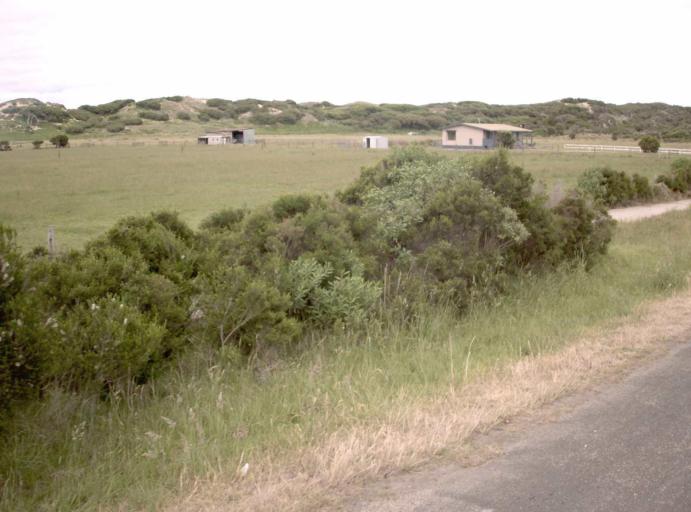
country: AU
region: Victoria
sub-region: Bass Coast
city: Phillip Island
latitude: -38.5152
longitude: 145.3113
